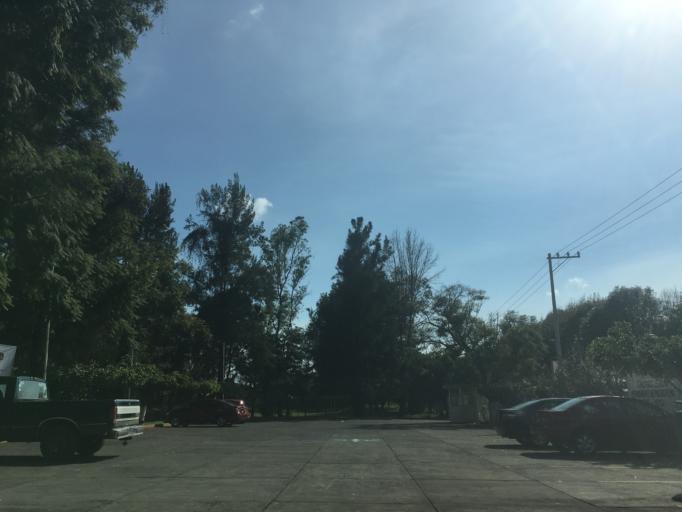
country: MX
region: Michoacan
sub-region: Uruapan
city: Uruapan
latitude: 19.4131
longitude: -102.0470
